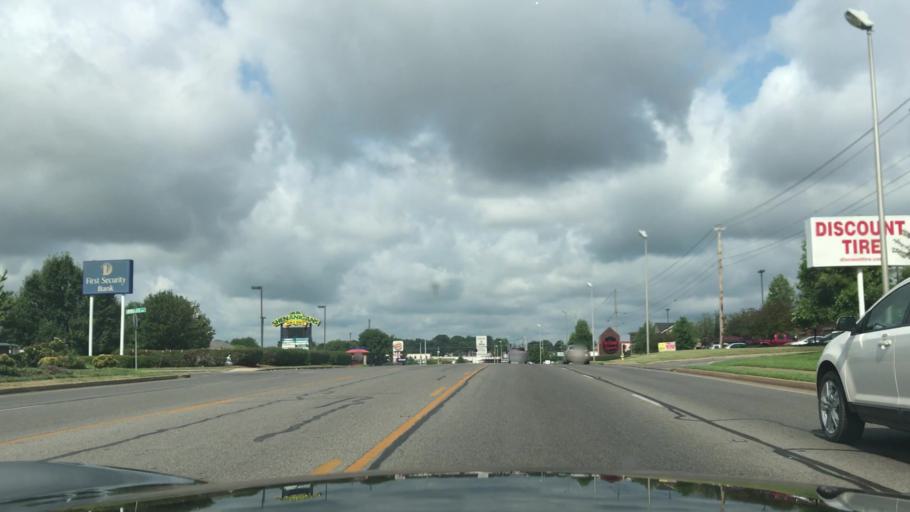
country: US
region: Kentucky
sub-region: Warren County
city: Bowling Green
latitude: 36.9616
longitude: -86.4625
